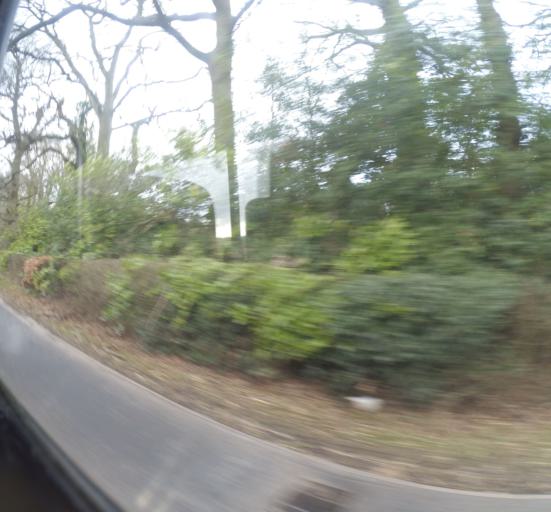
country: GB
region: England
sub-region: Warwickshire
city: Long Lawford
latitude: 52.4094
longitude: -1.3383
